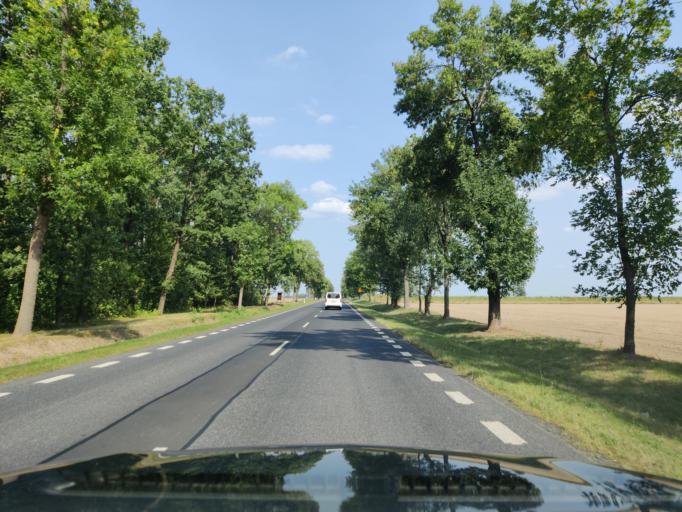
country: PL
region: Masovian Voivodeship
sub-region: Powiat makowski
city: Rzewnie
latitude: 52.8564
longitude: 21.3035
